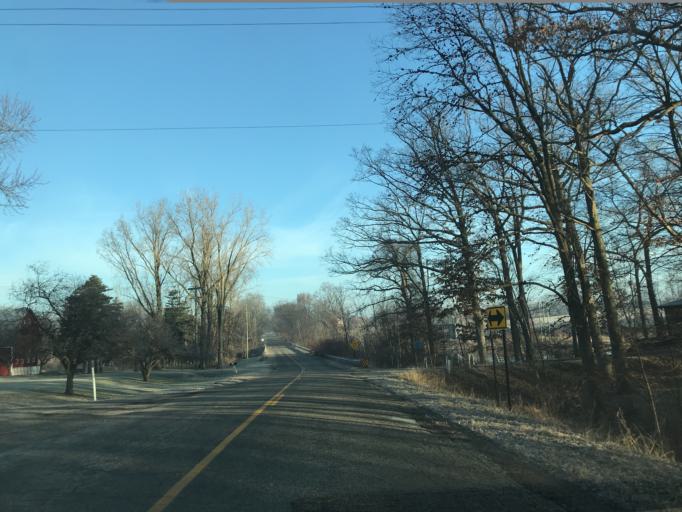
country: US
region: Michigan
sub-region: Eaton County
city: Eaton Rapids
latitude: 42.4872
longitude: -84.6011
